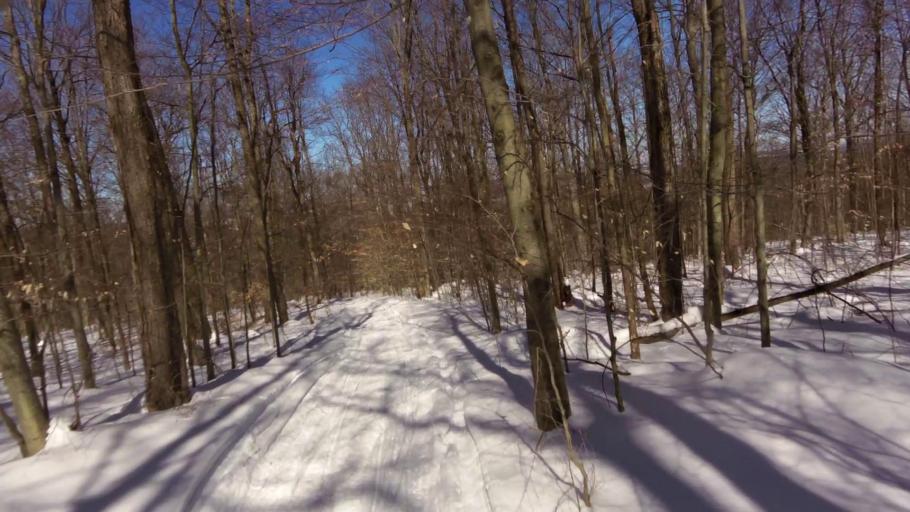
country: US
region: New York
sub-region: Allegany County
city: Houghton
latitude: 42.3621
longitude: -78.1854
